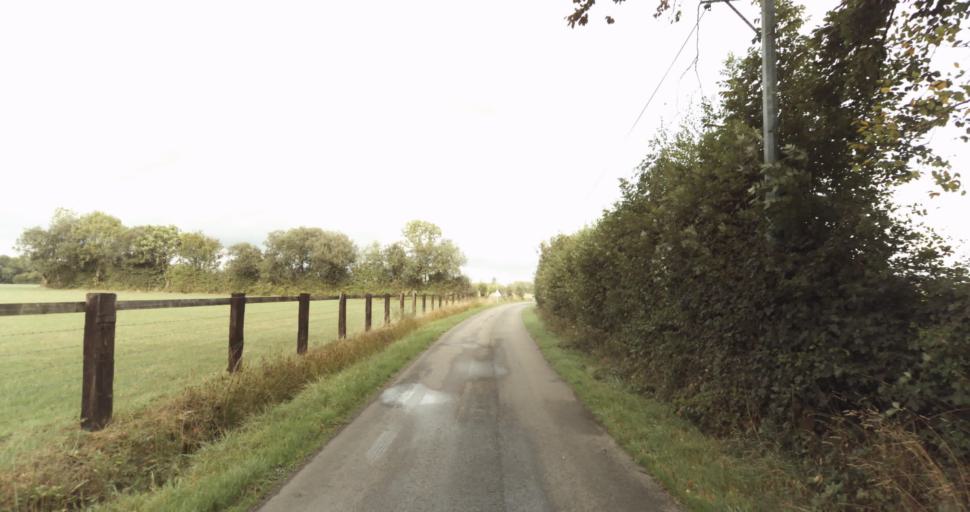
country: FR
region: Lower Normandy
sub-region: Departement de l'Orne
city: Sainte-Gauburge-Sainte-Colombe
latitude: 48.6884
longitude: 0.3304
